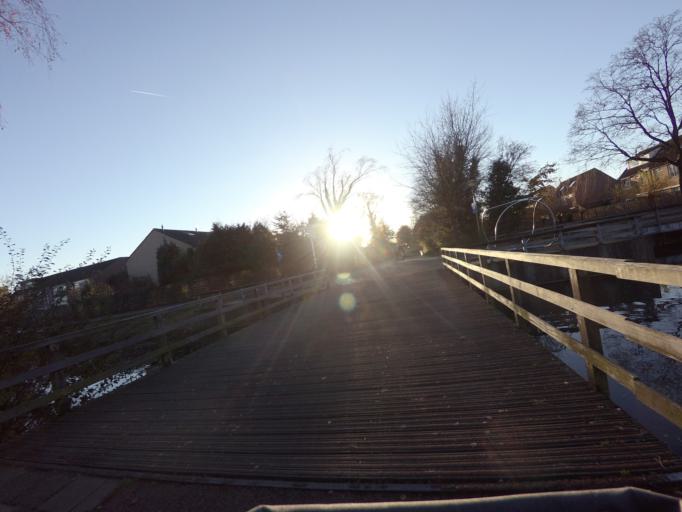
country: NL
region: Utrecht
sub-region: Stichtse Vecht
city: Spechtenkamp
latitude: 52.1338
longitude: 5.0236
